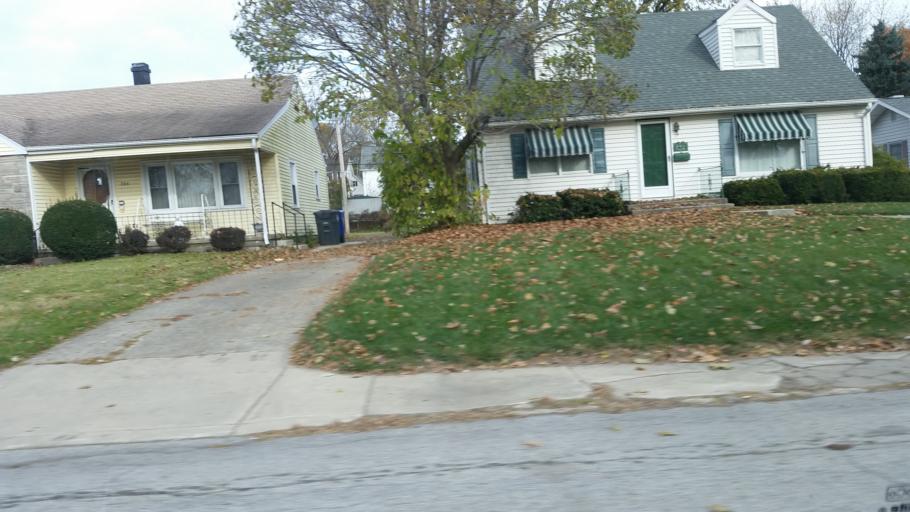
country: US
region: Indiana
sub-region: Howard County
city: Kokomo
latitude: 40.4854
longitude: -86.1387
